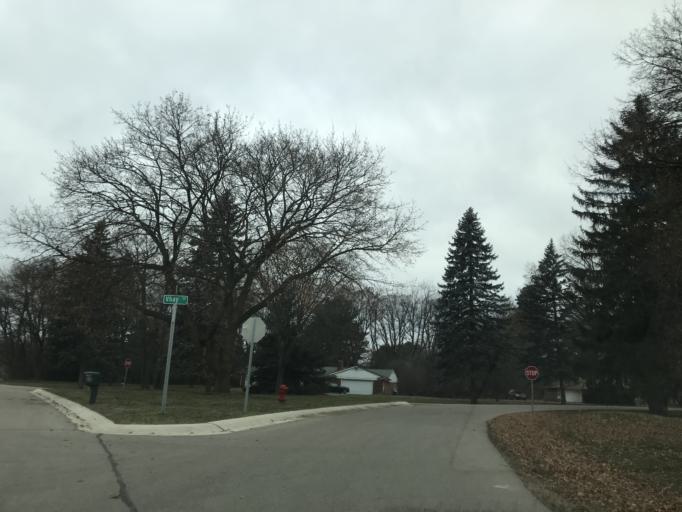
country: US
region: Michigan
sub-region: Oakland County
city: Bloomfield Hills
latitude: 42.6017
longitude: -83.2114
